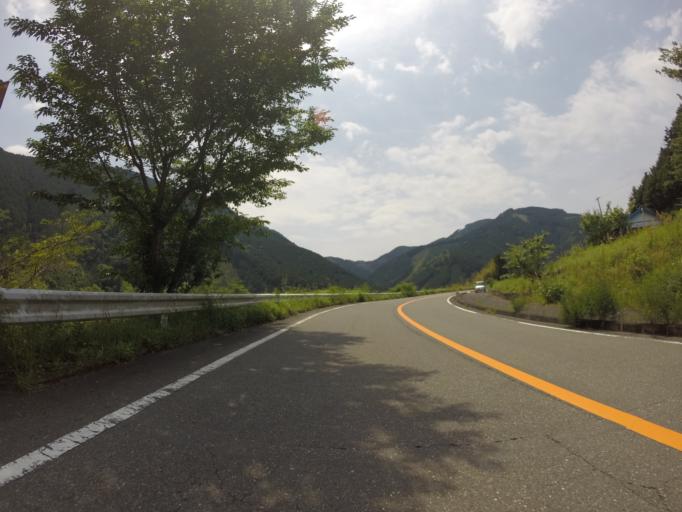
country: JP
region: Shizuoka
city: Shizuoka-shi
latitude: 35.1110
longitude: 138.3454
